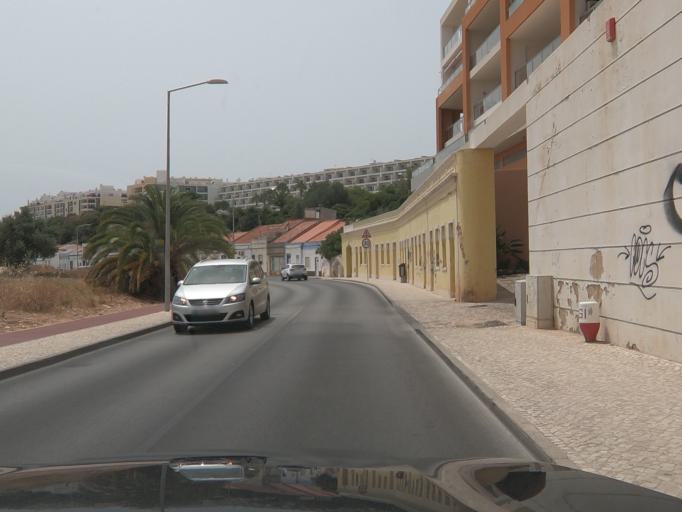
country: PT
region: Faro
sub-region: Portimao
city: Portimao
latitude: 37.1273
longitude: -8.5341
